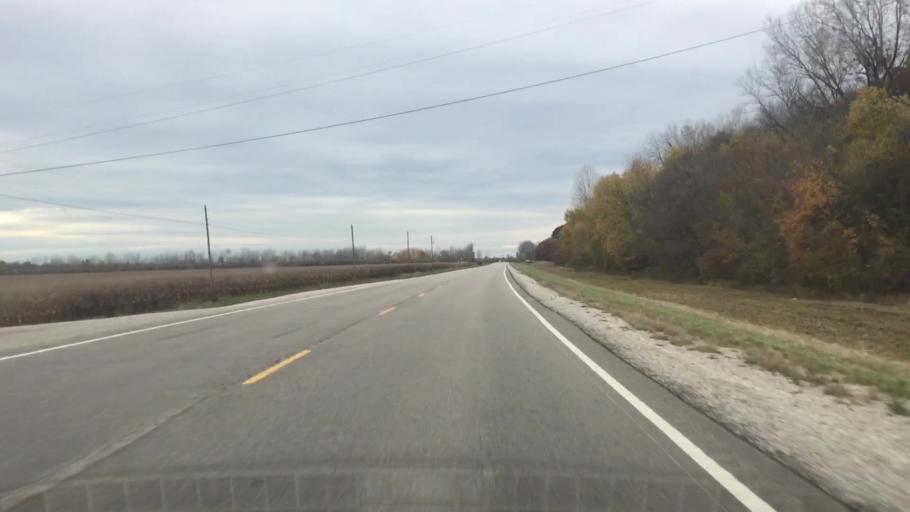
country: US
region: Missouri
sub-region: Callaway County
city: Holts Summit
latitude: 38.5808
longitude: -92.1002
